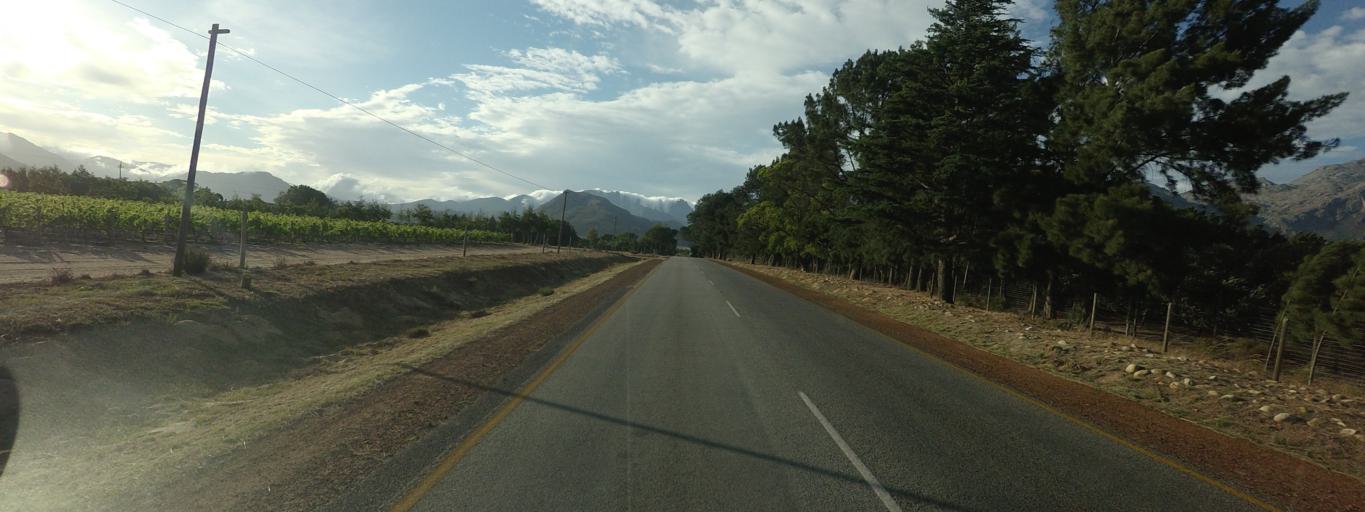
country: ZA
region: Western Cape
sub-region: Cape Winelands District Municipality
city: Paarl
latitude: -33.8679
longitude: 19.0419
